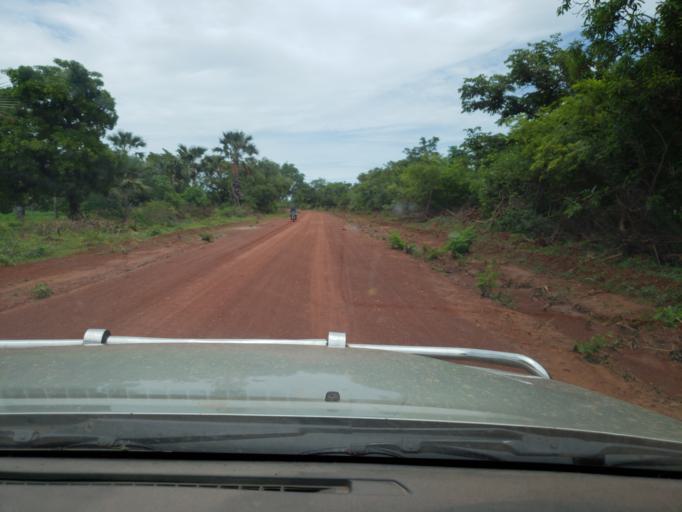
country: ML
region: Sikasso
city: Sikasso
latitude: 11.6592
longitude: -6.3421
